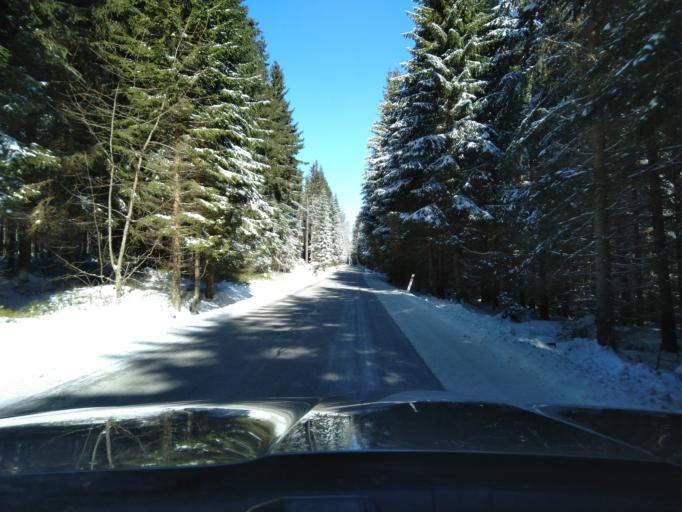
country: CZ
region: Jihocesky
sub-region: Okres Prachatice
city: Zdikov
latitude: 49.0511
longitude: 13.6614
